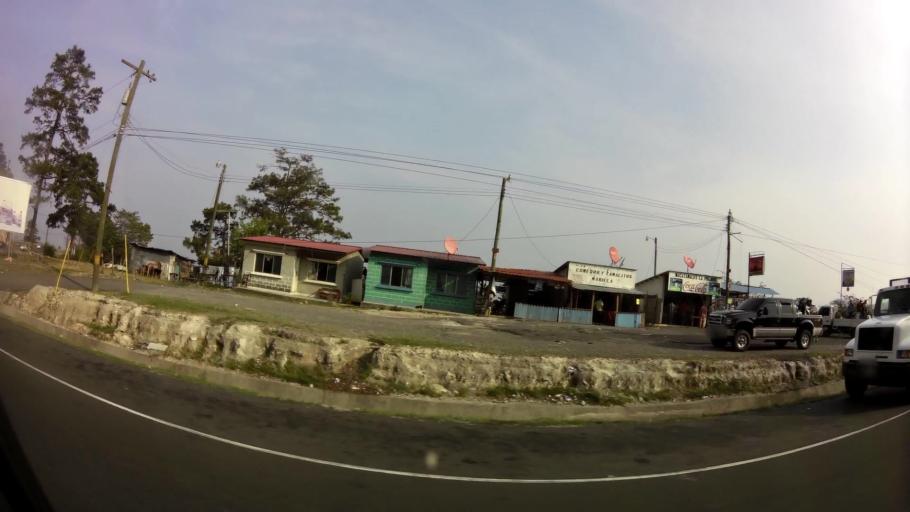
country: HN
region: Comayagua
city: Flores
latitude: 14.2912
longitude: -87.4890
